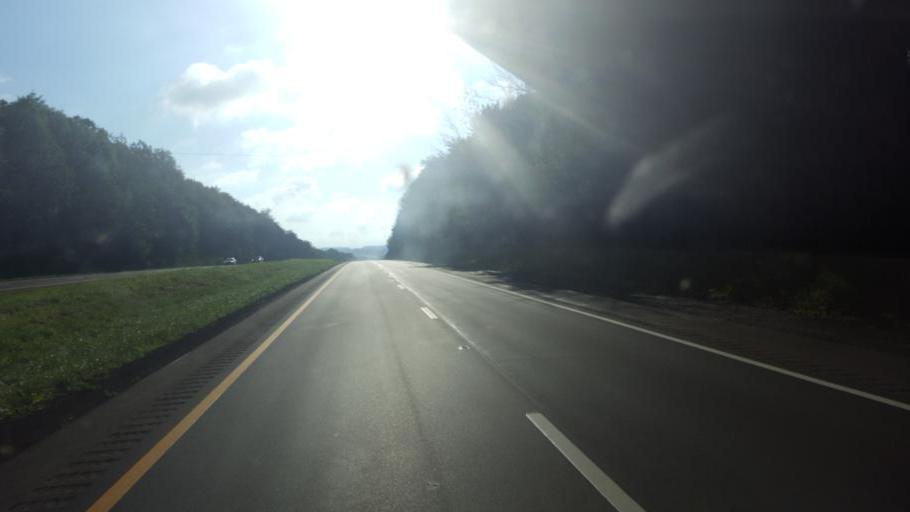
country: US
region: Ohio
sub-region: Wayne County
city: Shreve
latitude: 40.7841
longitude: -82.1356
